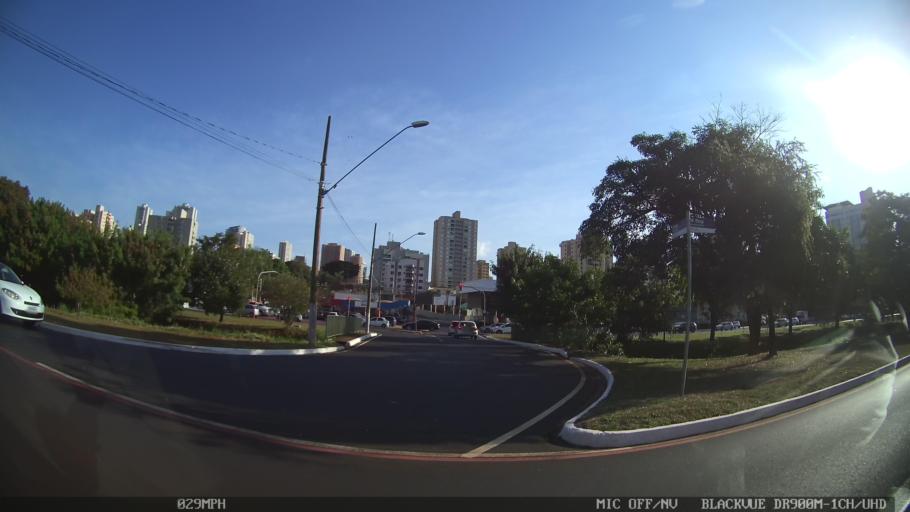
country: BR
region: Sao Paulo
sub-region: Ribeirao Preto
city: Ribeirao Preto
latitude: -21.2029
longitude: -47.7936
